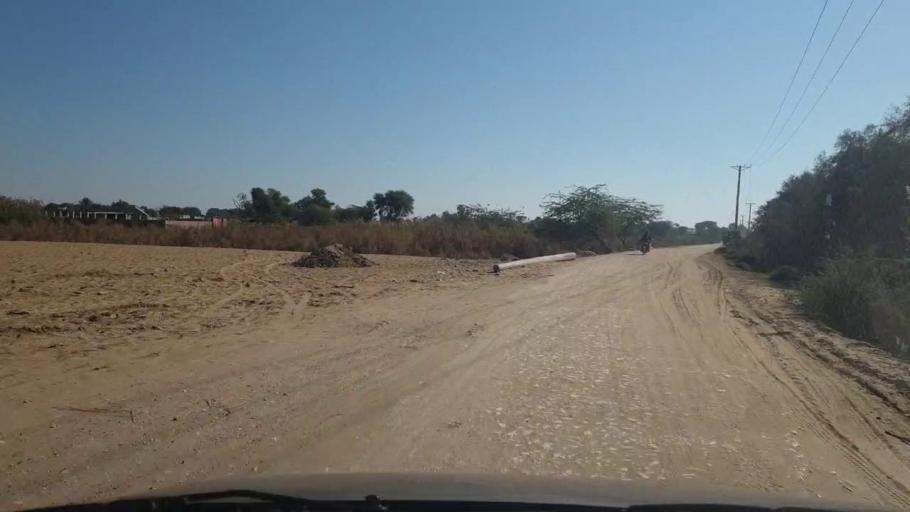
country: PK
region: Sindh
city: Bozdar
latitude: 27.0746
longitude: 68.6155
